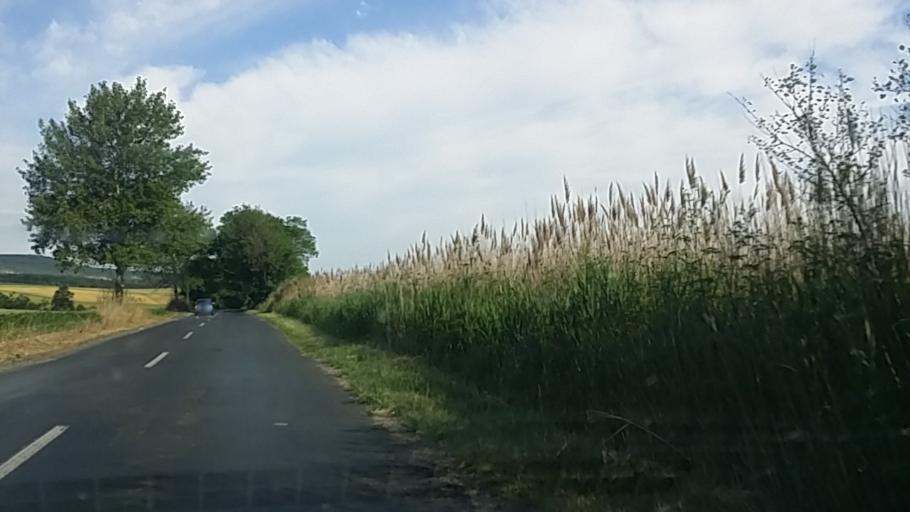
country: HU
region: Komarom-Esztergom
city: Bajna
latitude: 47.6911
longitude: 18.5635
